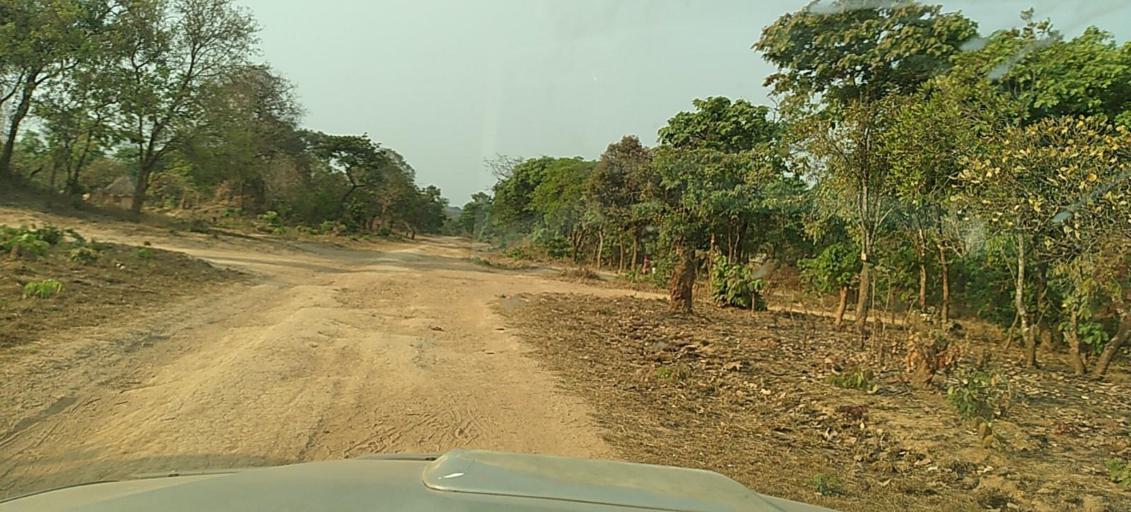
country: ZM
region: North-Western
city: Kasempa
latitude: -13.2748
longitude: 26.5562
